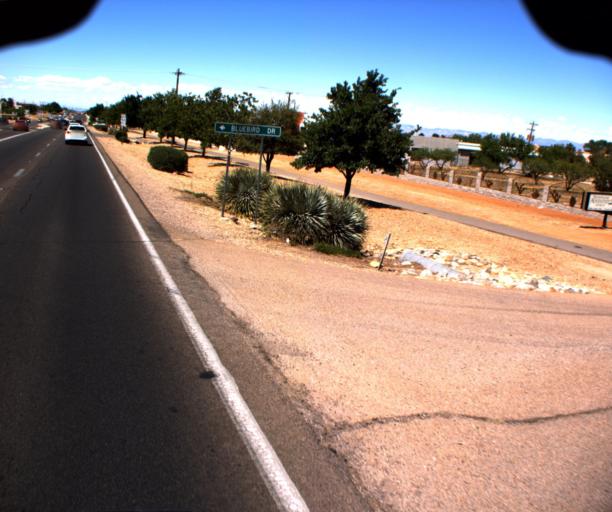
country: US
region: Arizona
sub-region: Cochise County
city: Sierra Vista
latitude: 31.5465
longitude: -110.2573
